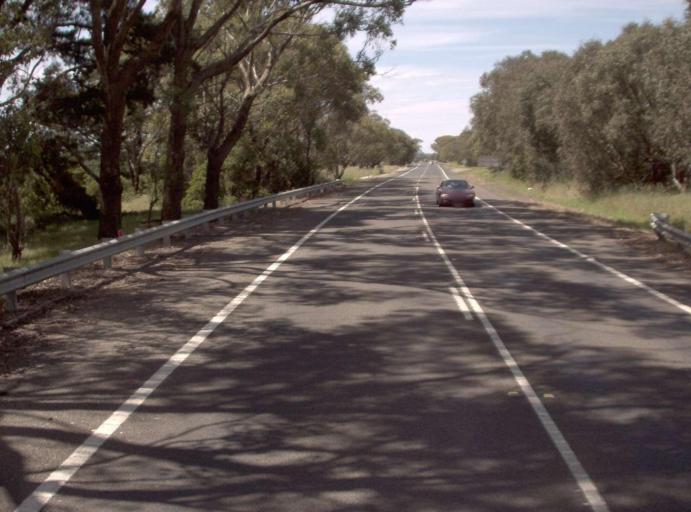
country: AU
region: Victoria
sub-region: Wellington
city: Sale
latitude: -37.9875
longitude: 147.0675
